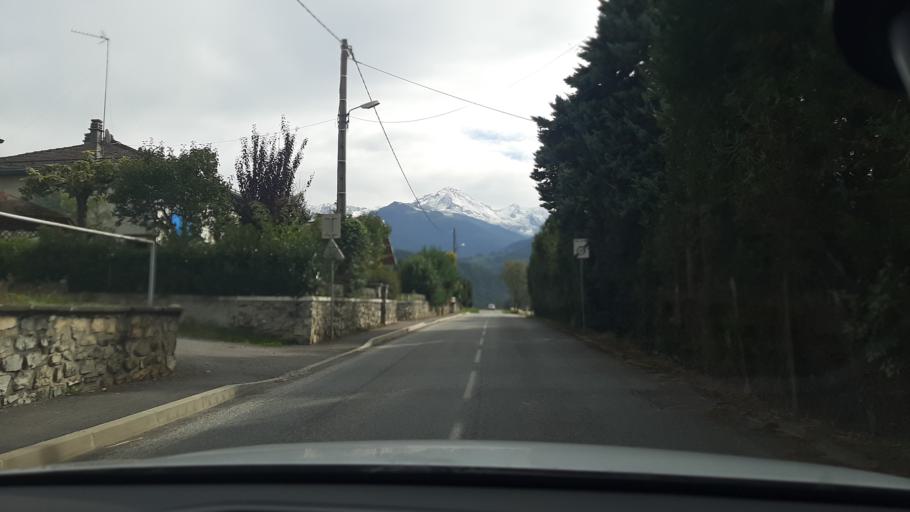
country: FR
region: Rhone-Alpes
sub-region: Departement de la Savoie
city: La Rochette
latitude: 45.4470
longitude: 6.0728
